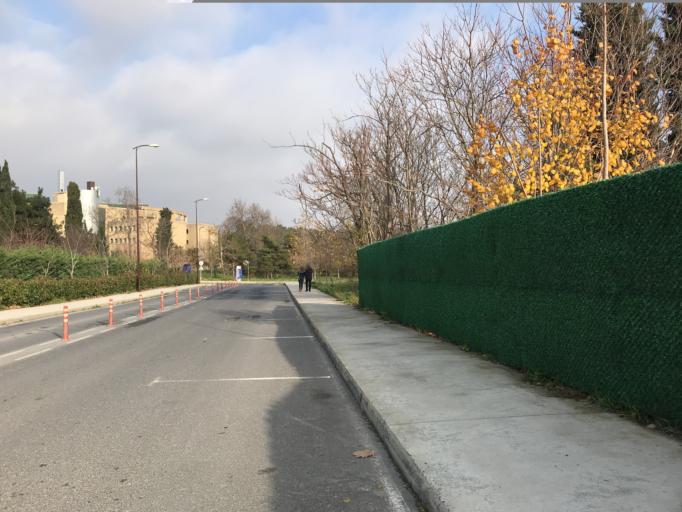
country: TR
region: Istanbul
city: merter keresteciler
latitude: 41.0202
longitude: 28.8921
